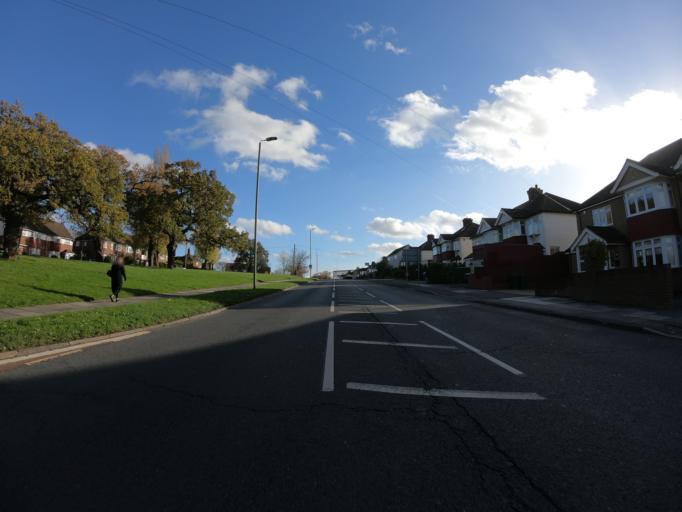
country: GB
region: England
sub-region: Greater London
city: Chislehurst
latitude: 51.4269
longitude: 0.0556
